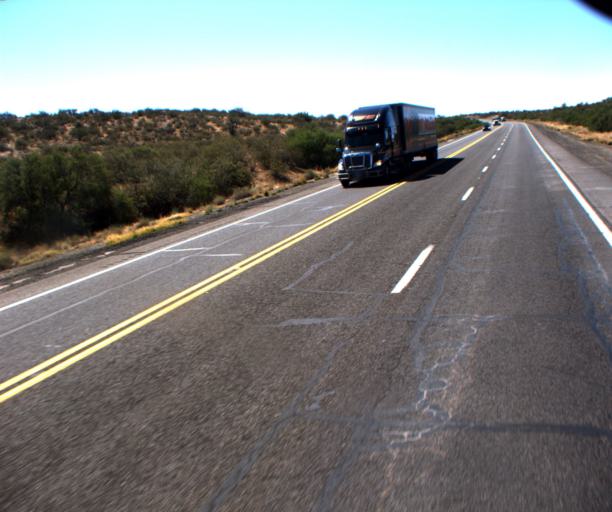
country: US
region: Arizona
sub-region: Yavapai County
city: Congress
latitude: 34.2010
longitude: -113.0618
